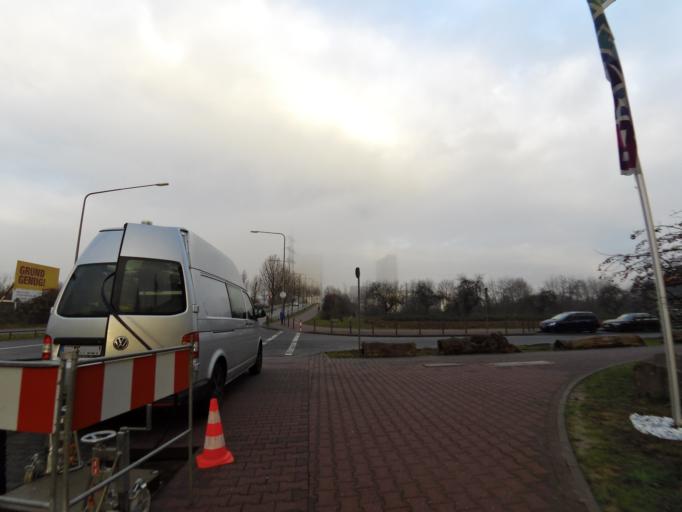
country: DE
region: Hesse
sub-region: Regierungsbezirk Darmstadt
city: Eschborn
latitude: 50.1288
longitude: 8.5789
